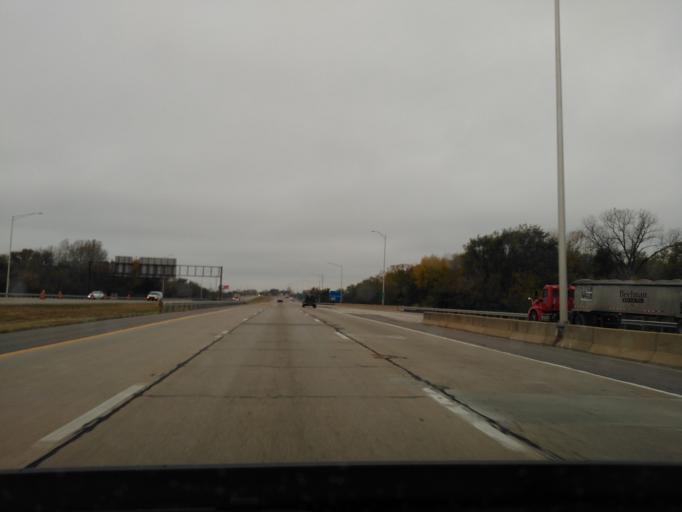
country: US
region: Illinois
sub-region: Saint Clair County
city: Washington Park
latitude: 38.6141
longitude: -90.0736
